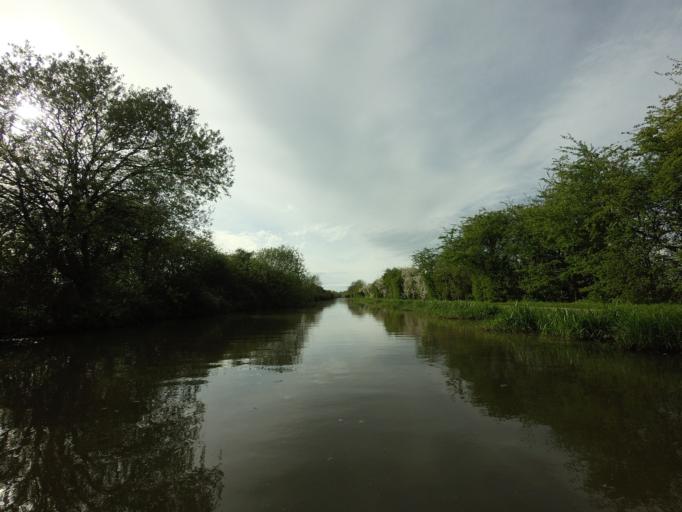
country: GB
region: England
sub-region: Milton Keynes
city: Stony Stratford
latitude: 52.0667
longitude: -0.8297
